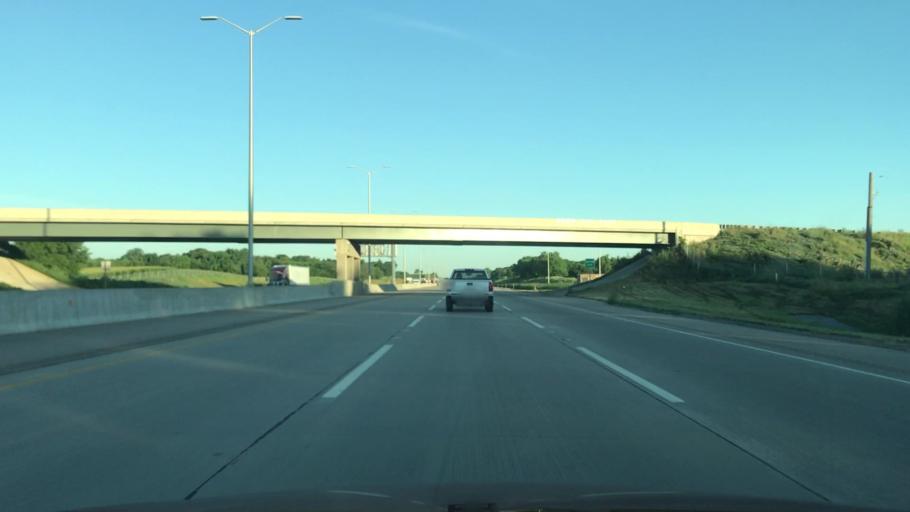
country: US
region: Illinois
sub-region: McHenry County
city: Huntley
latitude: 42.1362
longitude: -88.4806
